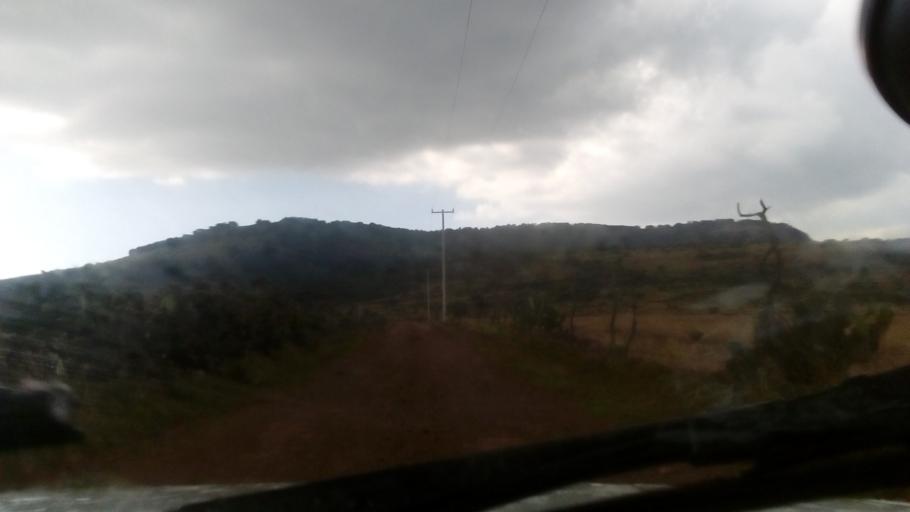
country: MX
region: Guanajuato
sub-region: Silao de la Victoria
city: San Francisco (Banos de Agua Caliente)
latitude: 21.1601
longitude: -101.4310
